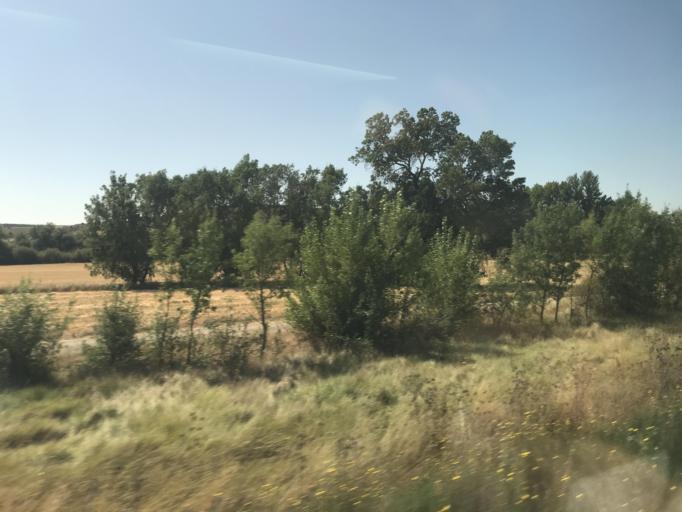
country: ES
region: Castille and Leon
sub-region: Provincia de Burgos
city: Celada del Camino
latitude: 42.2566
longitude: -3.9342
